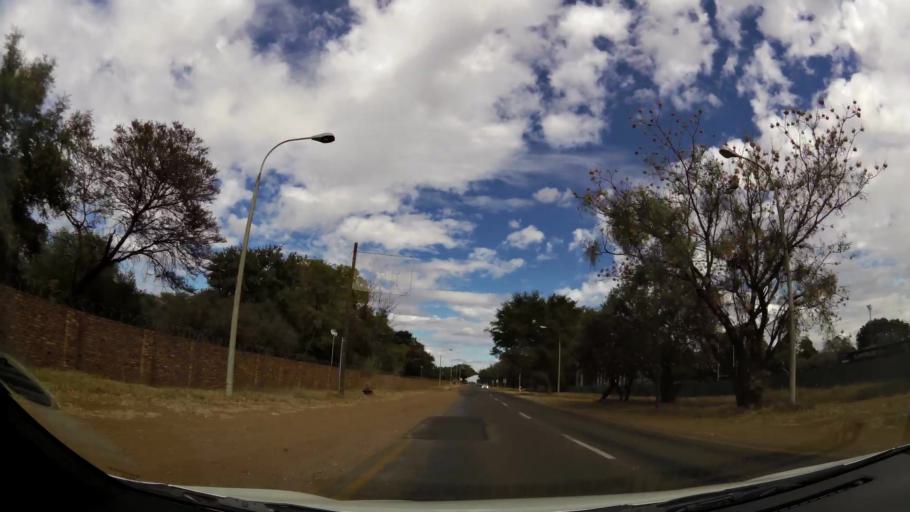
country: ZA
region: Limpopo
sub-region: Waterberg District Municipality
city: Warmbaths
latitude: -24.8894
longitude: 28.2840
